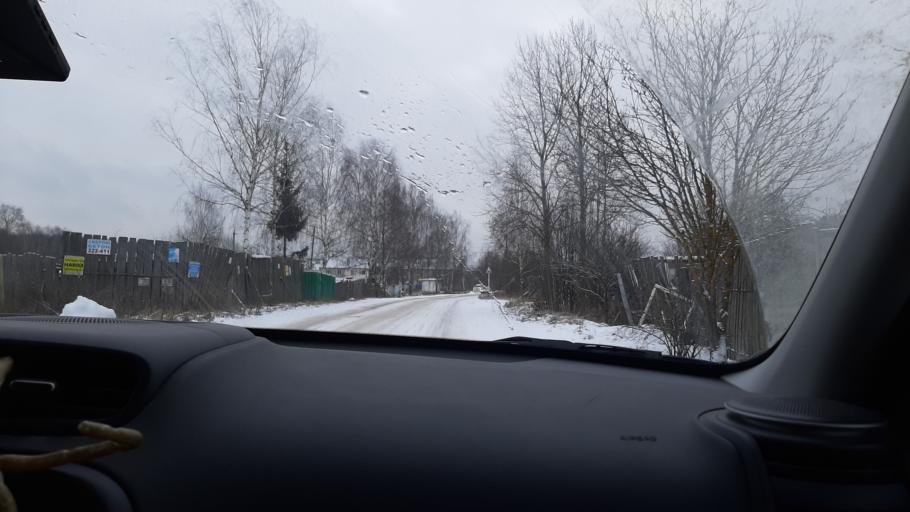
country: RU
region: Ivanovo
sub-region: Gorod Ivanovo
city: Ivanovo
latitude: 56.9280
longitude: 40.9811
